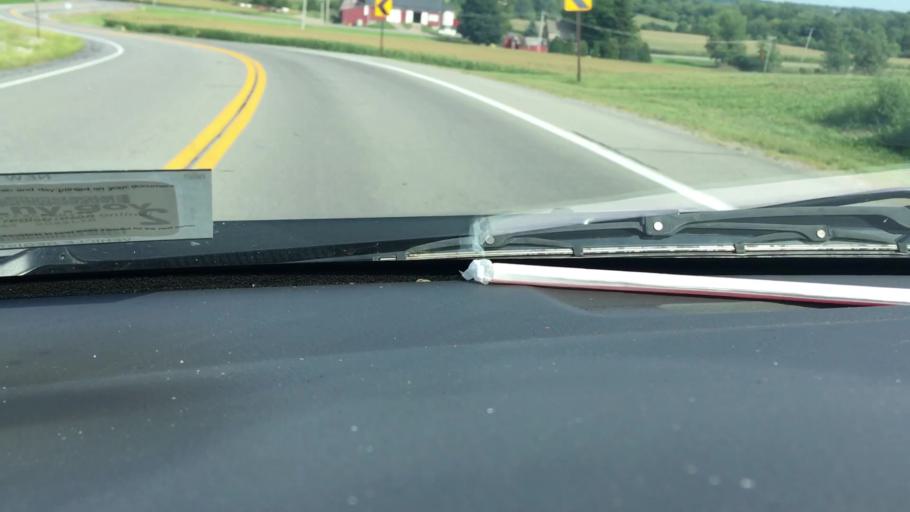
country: US
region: New York
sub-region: Genesee County
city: Batavia
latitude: 43.0147
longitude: -78.1375
